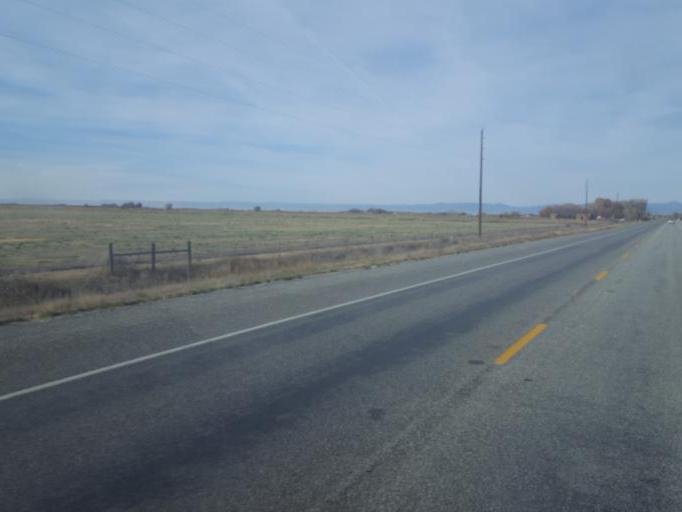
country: US
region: Colorado
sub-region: Alamosa County
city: Alamosa East
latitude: 37.4737
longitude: -105.7766
